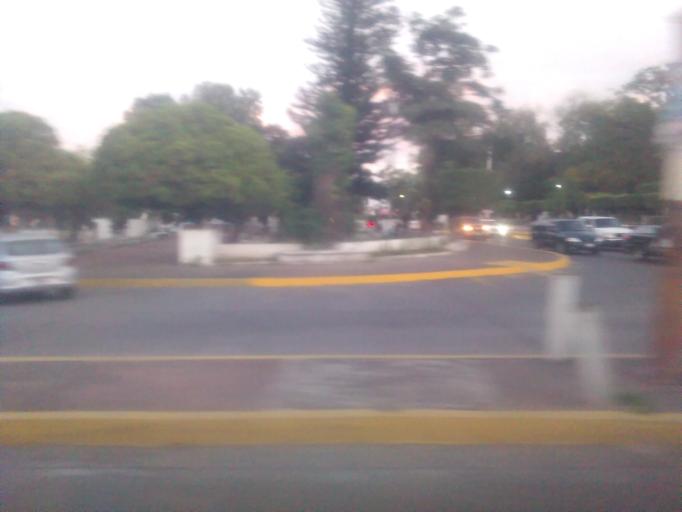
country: MX
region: Nayarit
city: Tepic
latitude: 21.5120
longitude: -104.9007
